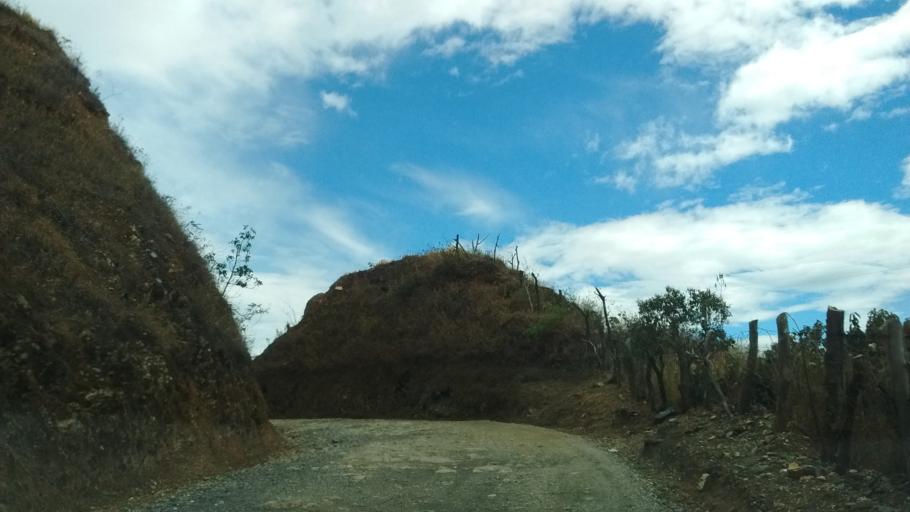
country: CO
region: Cauca
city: Almaguer
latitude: 1.8447
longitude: -76.9119
